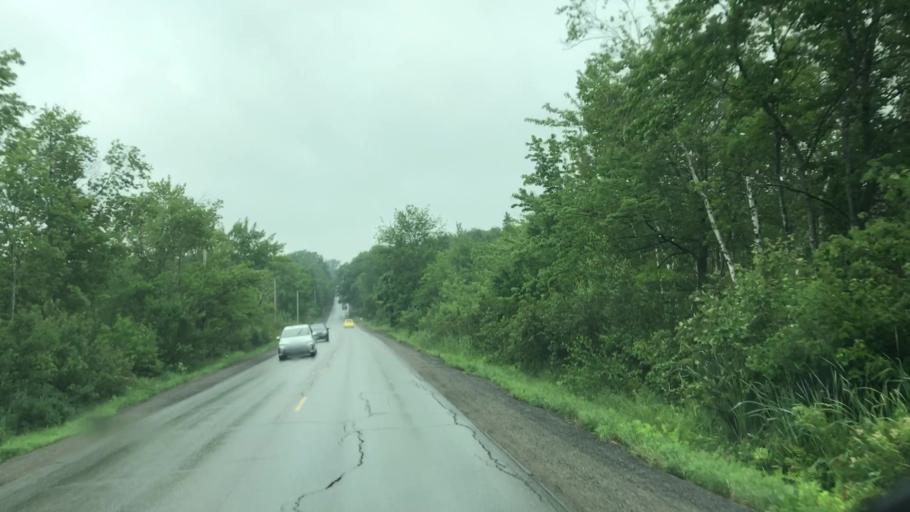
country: US
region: Maine
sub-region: Penobscot County
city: Veazie
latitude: 44.8725
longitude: -68.7145
